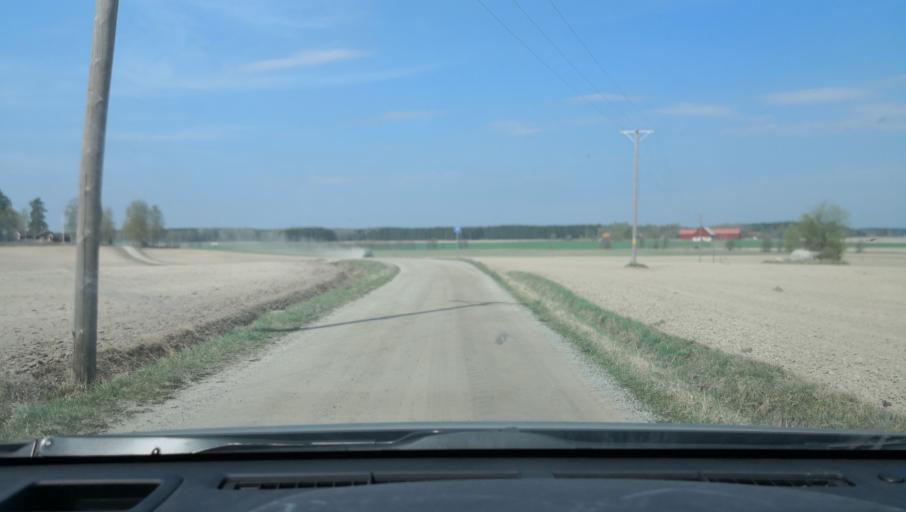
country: SE
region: Vaestmanland
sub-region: Vasteras
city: Skultuna
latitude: 59.7739
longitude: 16.4383
